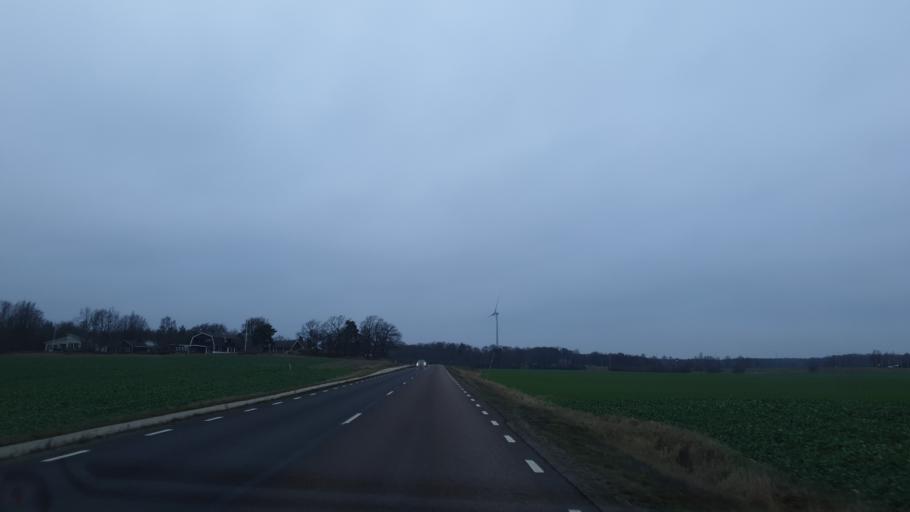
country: SE
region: Blekinge
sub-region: Karlskrona Kommun
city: Jaemjoe
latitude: 56.1781
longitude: 15.7209
